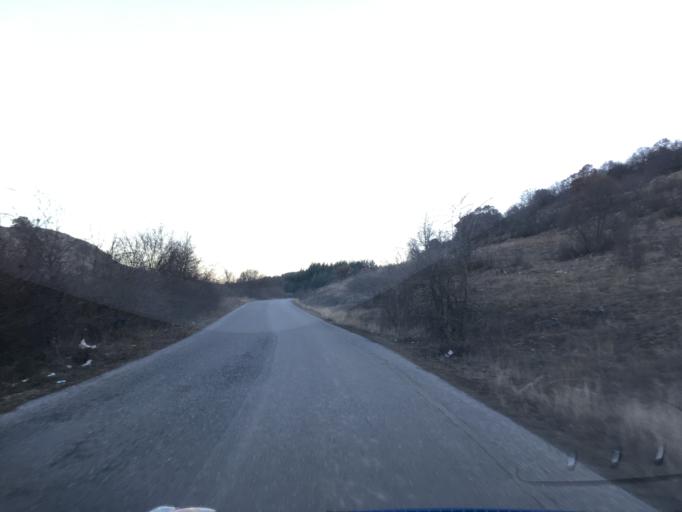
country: GR
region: West Macedonia
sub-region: Nomos Kozanis
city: Koila
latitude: 40.3275
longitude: 21.8122
